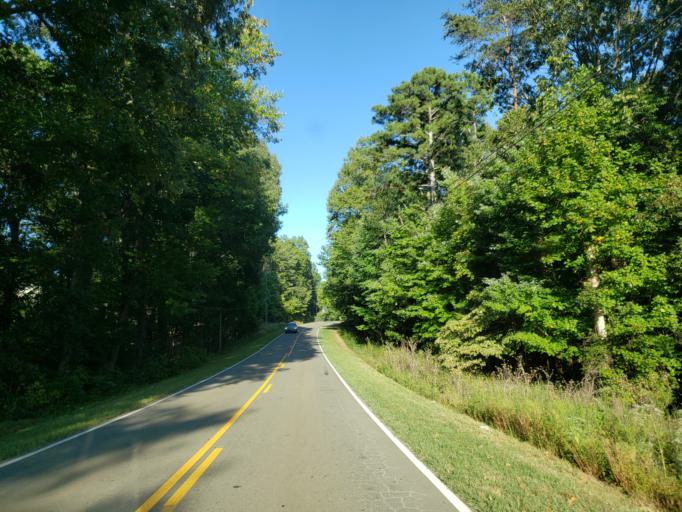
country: US
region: Georgia
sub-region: Pickens County
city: Nelson
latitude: 34.4034
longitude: -84.3910
